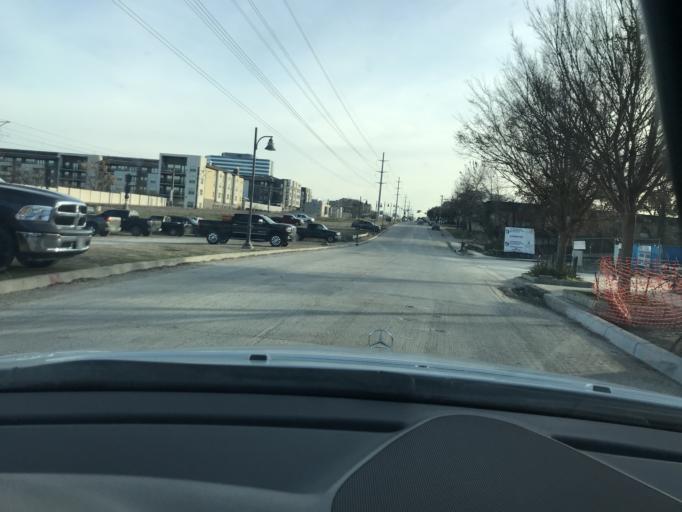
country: US
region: Texas
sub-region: Dallas County
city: University Park
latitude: 32.8905
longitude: -96.7652
